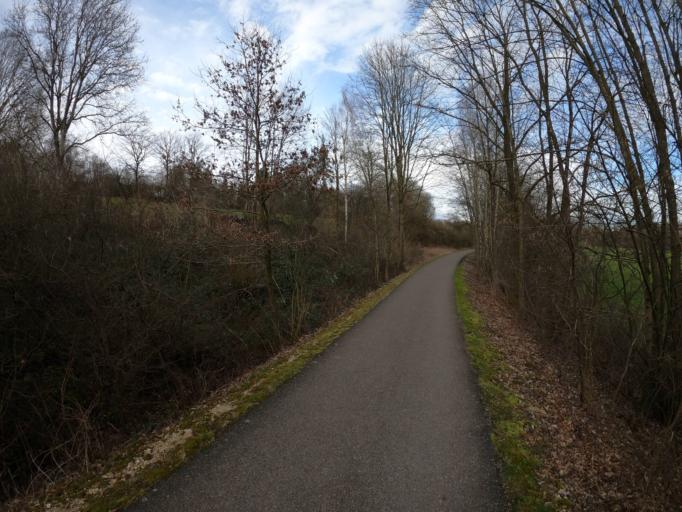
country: DE
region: Baden-Wuerttemberg
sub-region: Regierungsbezirk Stuttgart
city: Rechberghausen
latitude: 48.7197
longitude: 9.6316
